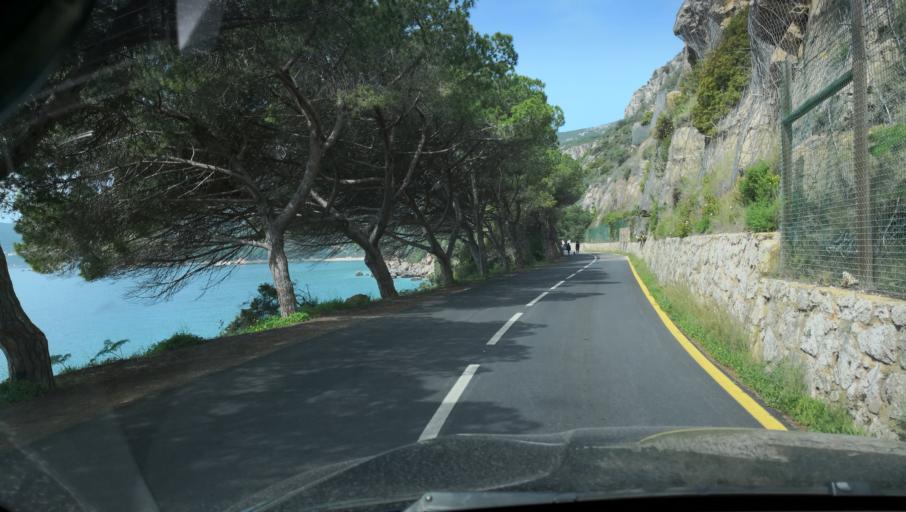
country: PT
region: Setubal
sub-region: Setubal
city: Setubal
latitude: 38.4849
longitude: -8.9578
